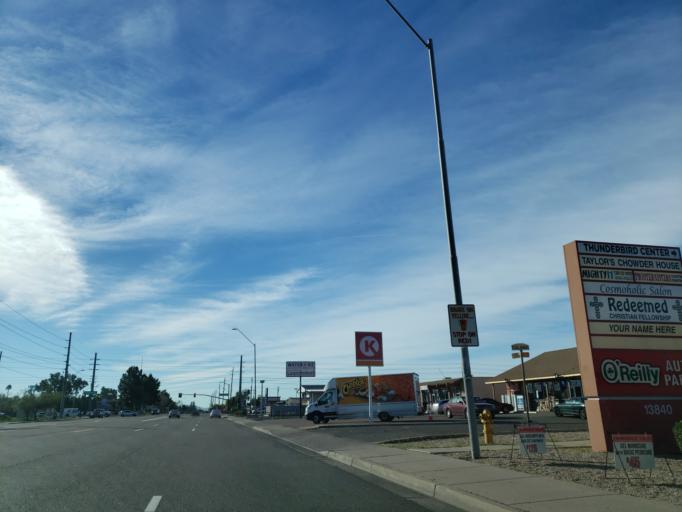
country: US
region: Arizona
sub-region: Maricopa County
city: Glendale
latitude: 33.6123
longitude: -112.1339
